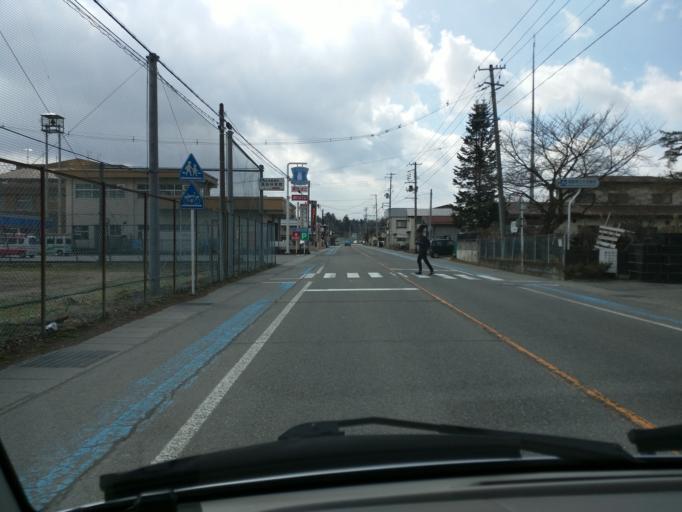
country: JP
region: Fukushima
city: Kitakata
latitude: 37.4628
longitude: 139.8438
